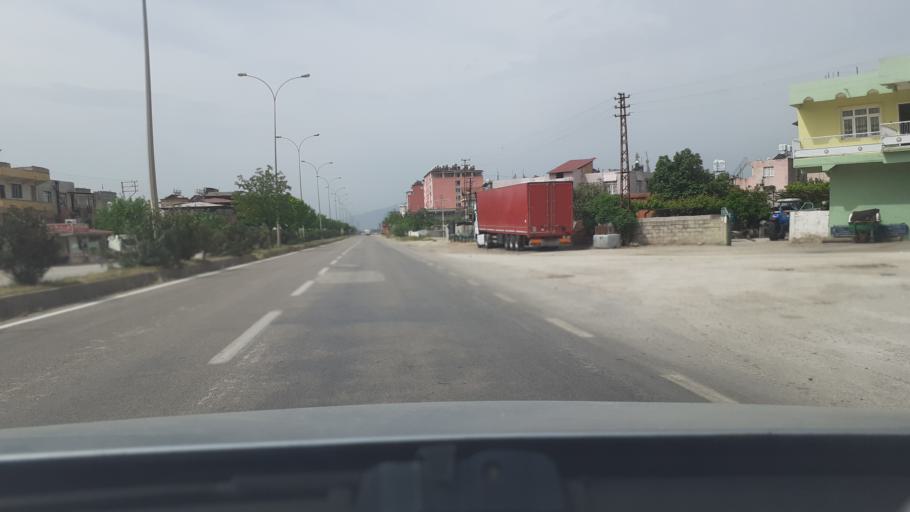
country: TR
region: Hatay
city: Kirikhan
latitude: 36.4837
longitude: 36.3612
